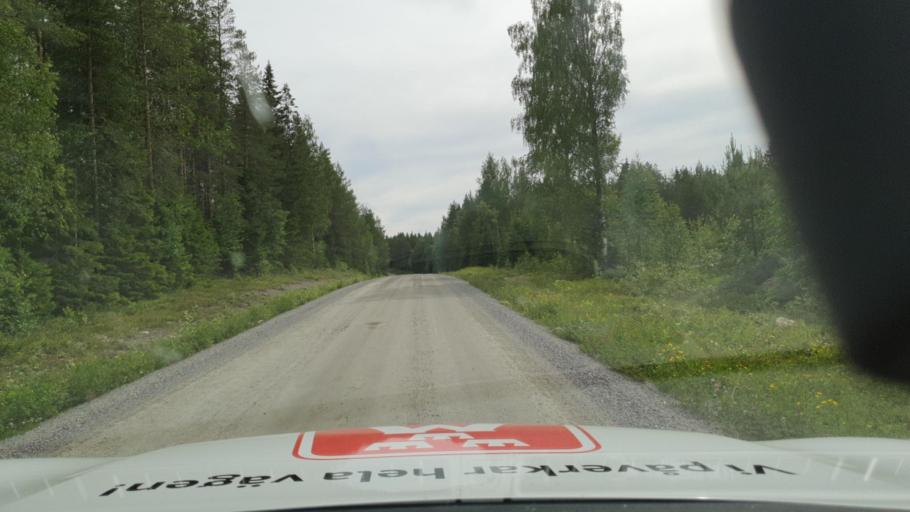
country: SE
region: Vaesterbotten
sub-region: Skelleftea Kommun
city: Burea
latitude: 64.4432
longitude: 21.0196
